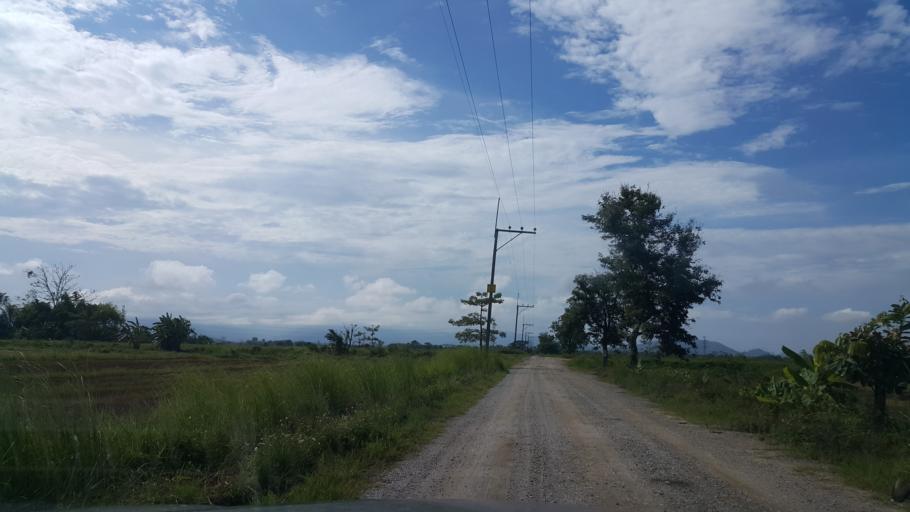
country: TH
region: Chiang Rai
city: Wiang Chai
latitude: 19.9540
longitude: 99.9296
